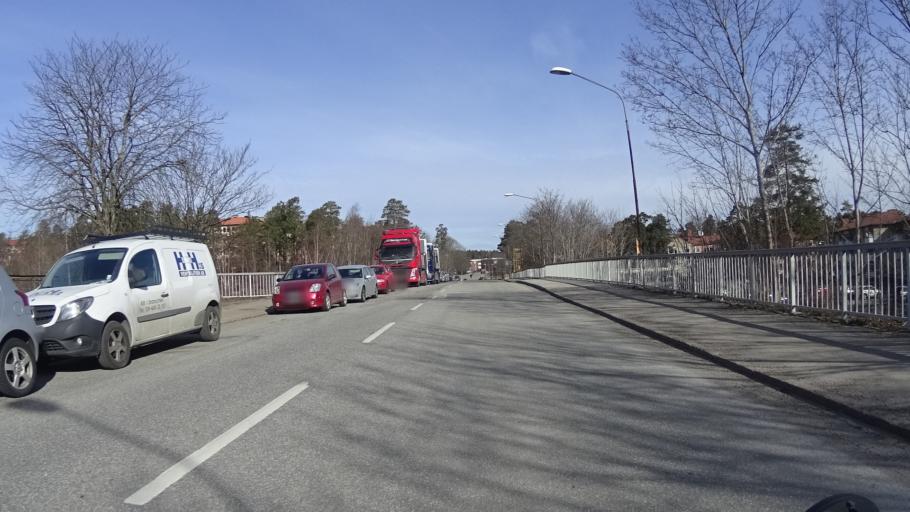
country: SE
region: Stockholm
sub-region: Nacka Kommun
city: Nacka
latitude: 59.2774
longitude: 18.1273
